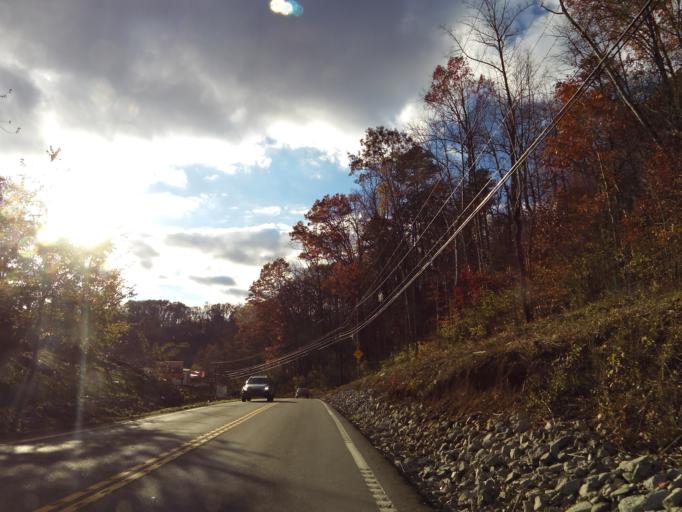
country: US
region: Tennessee
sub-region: Knox County
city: Knoxville
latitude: 35.9360
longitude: -83.9351
